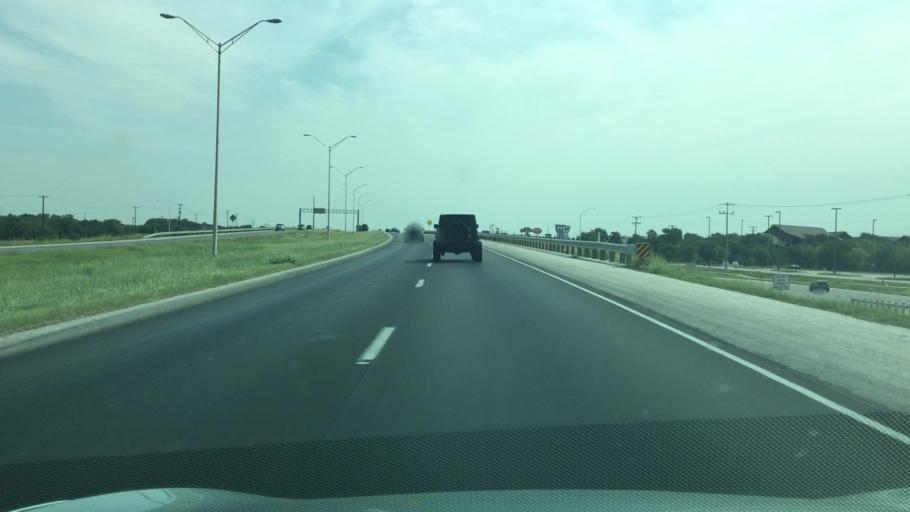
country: US
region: Texas
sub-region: Bexar County
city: Helotes
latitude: 29.5656
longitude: -98.6544
